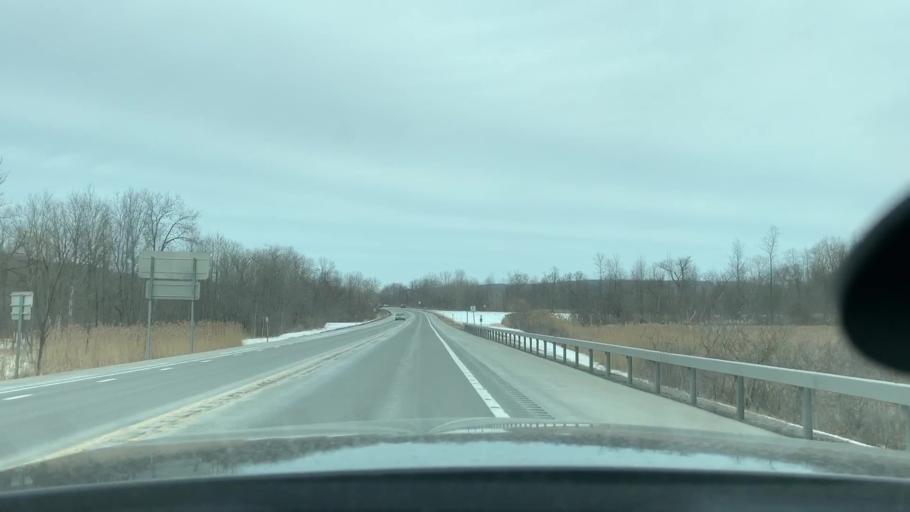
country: US
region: New York
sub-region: Herkimer County
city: Ilion
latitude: 43.0225
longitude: -75.0486
